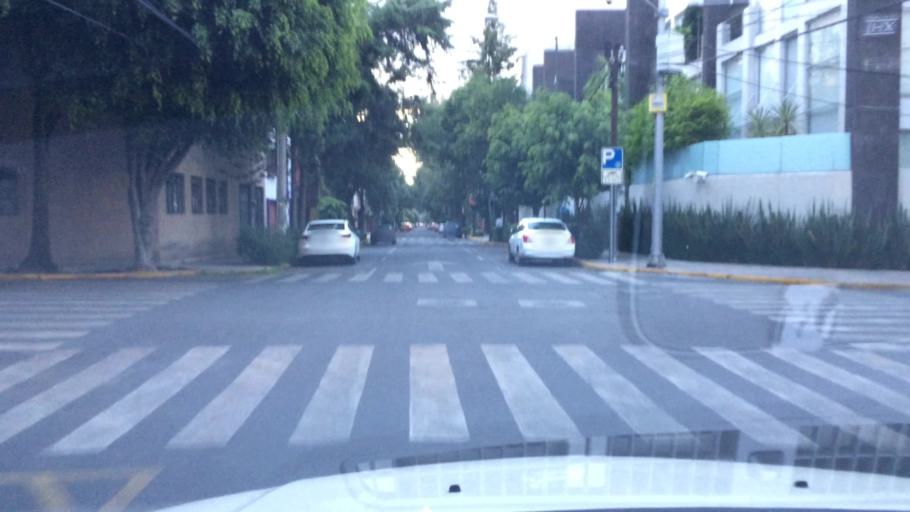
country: MX
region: Mexico City
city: Alvaro Obregon
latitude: 19.3658
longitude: -99.1866
